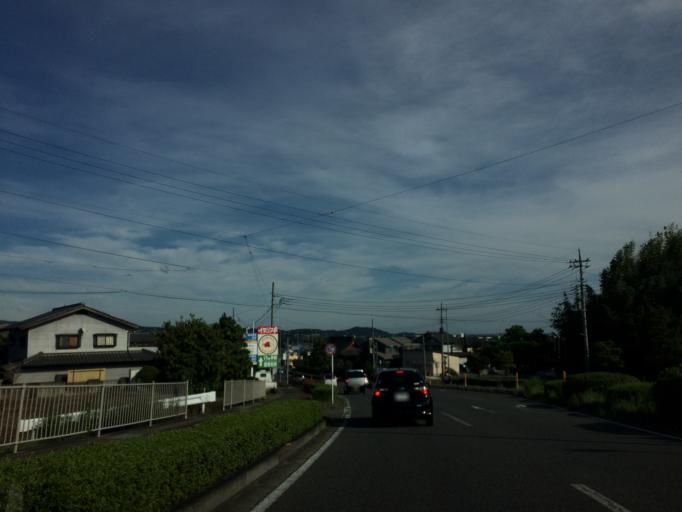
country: JP
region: Gunma
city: Shibukawa
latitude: 36.4842
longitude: 139.0006
